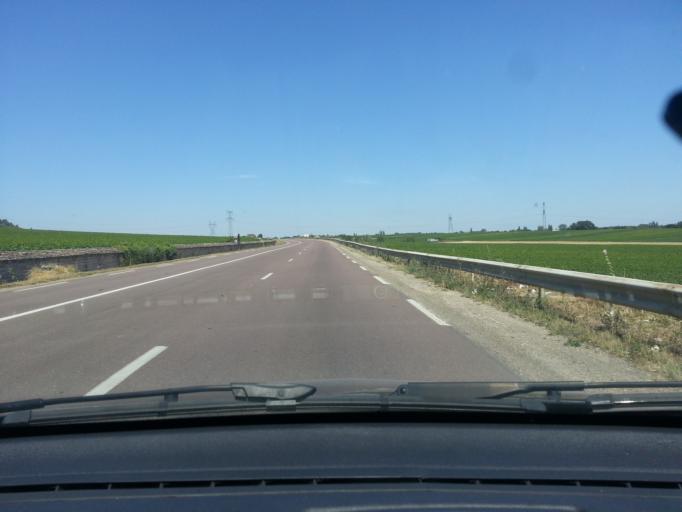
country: FR
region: Bourgogne
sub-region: Departement de la Cote-d'Or
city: Nuits-Saint-Georges
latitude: 47.1144
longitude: 4.9351
